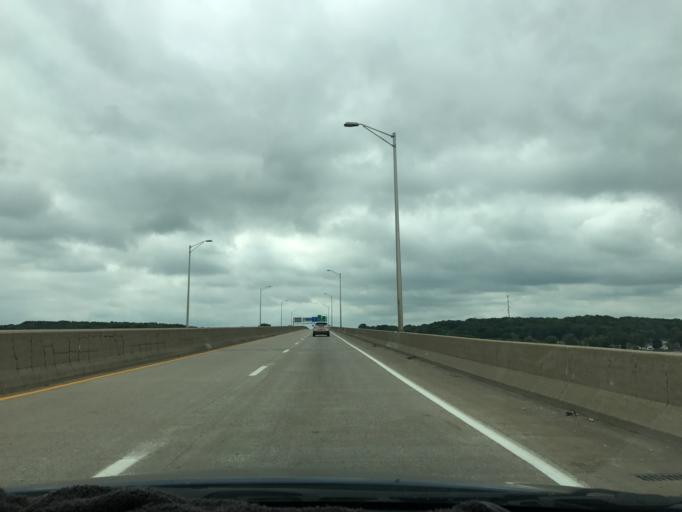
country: US
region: Iowa
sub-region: Scott County
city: Le Claire
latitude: 41.5835
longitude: -90.3670
